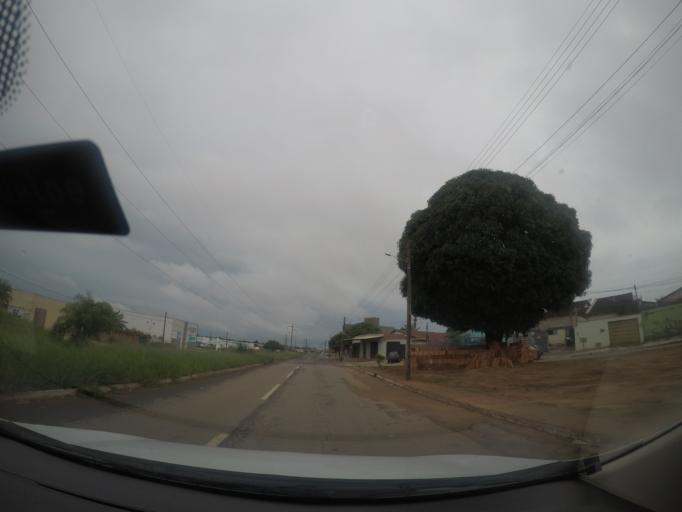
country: BR
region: Goias
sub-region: Aparecida De Goiania
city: Aparecida de Goiania
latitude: -16.7756
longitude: -49.2937
